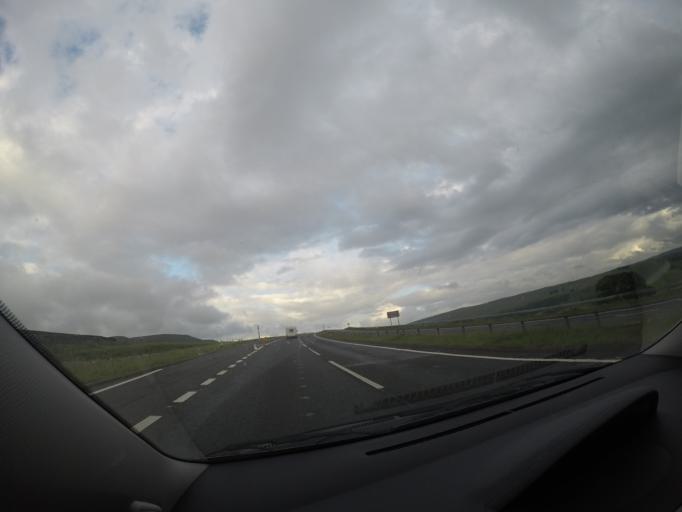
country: GB
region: England
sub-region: Cumbria
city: Kirkby Stephen
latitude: 54.5265
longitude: -2.2332
